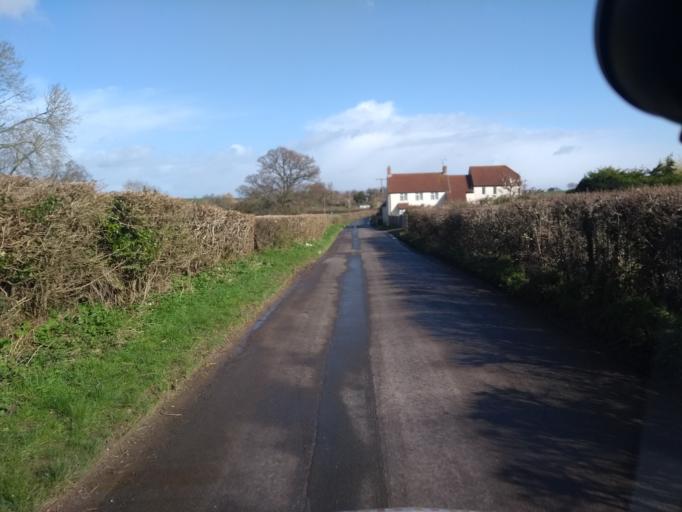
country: GB
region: England
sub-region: Somerset
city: South Petherton
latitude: 50.9592
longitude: -2.8389
